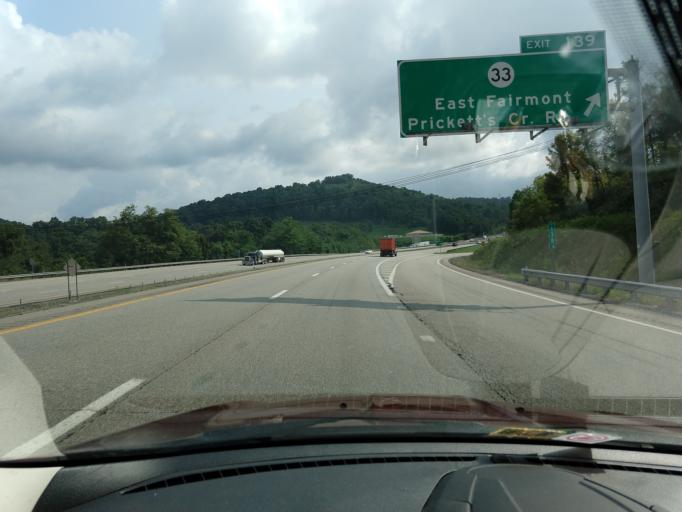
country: US
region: West Virginia
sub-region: Marion County
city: Fairmont
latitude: 39.4881
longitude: -80.0936
